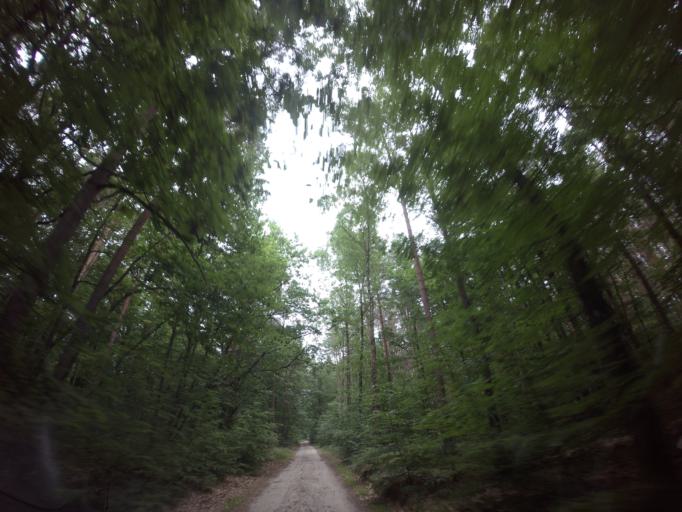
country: PL
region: Lubusz
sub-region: Powiat strzelecko-drezdenecki
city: Dobiegniew
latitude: 53.0779
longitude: 15.8090
